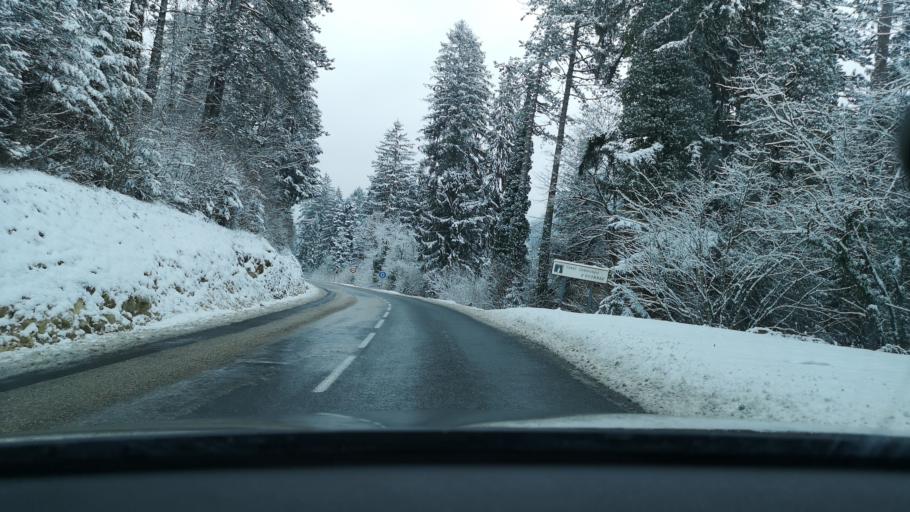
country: FR
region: Rhone-Alpes
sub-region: Departement de l'Ain
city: Oyonnax
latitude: 46.2554
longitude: 5.6680
